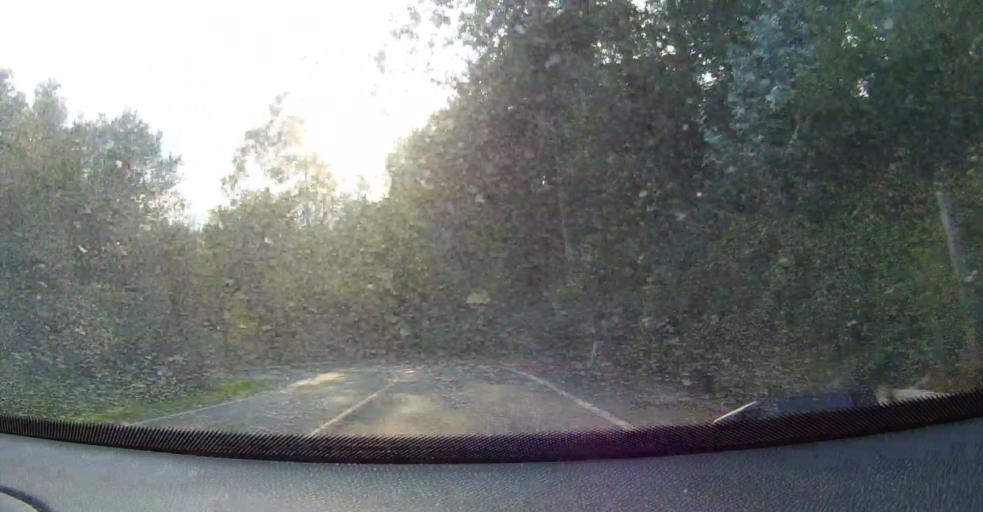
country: ES
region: Basque Country
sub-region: Bizkaia
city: Sopuerta
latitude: 43.2887
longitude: -3.1605
